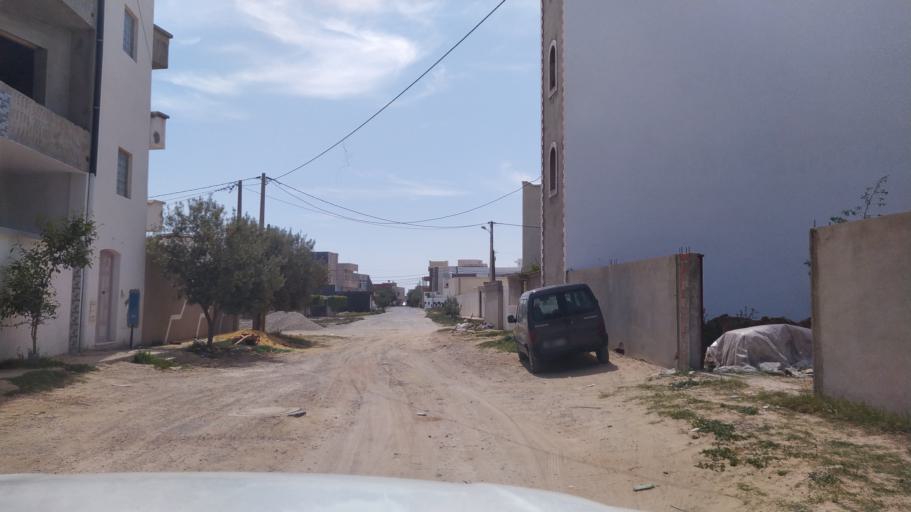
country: TN
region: Al Mahdiyah
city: Zouila
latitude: 35.5028
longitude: 11.0358
